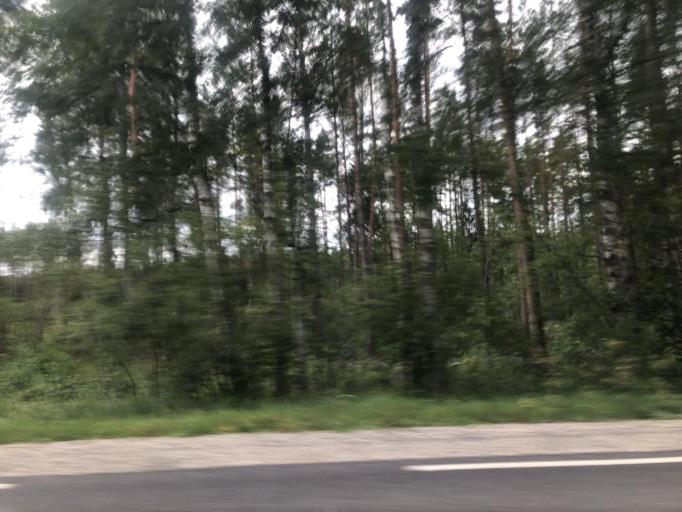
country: LV
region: Baldone
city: Baldone
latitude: 56.6739
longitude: 24.4097
